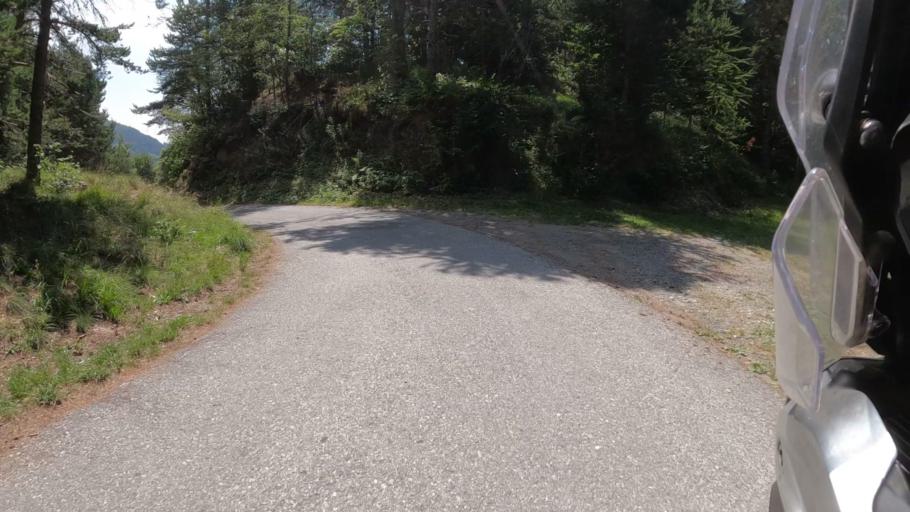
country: IT
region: Piedmont
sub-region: Provincia di Torino
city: Borgone Susa
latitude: 45.1554
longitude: 7.2627
